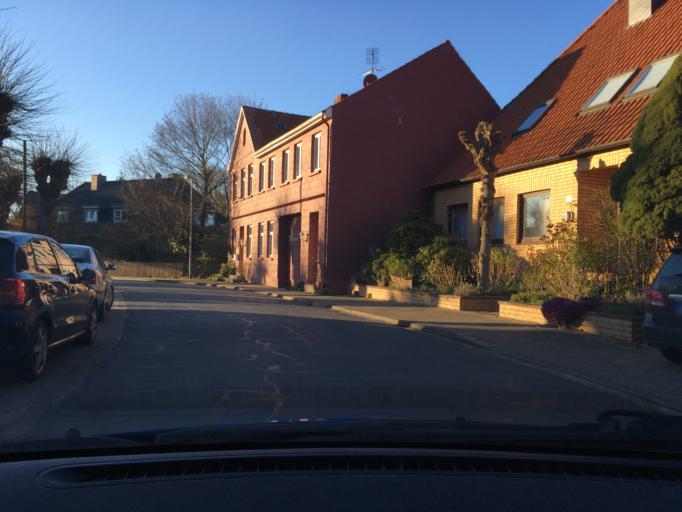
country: DE
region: Lower Saxony
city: Bleckede
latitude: 53.2938
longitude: 10.7309
